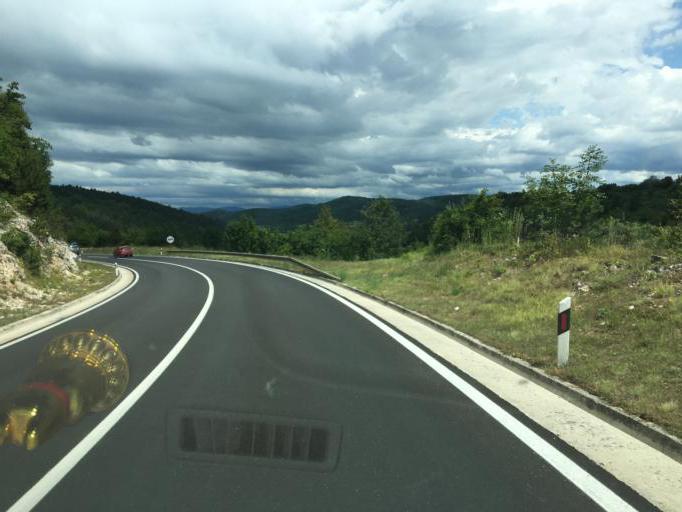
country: HR
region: Istarska
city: Pazin
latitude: 45.2468
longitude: 13.8796
